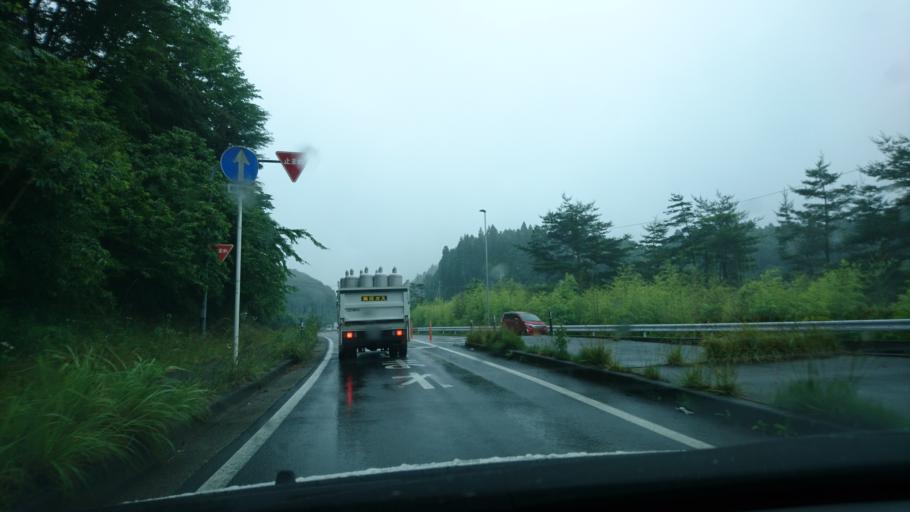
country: JP
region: Iwate
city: Ichinoseki
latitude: 38.8881
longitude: 141.1182
